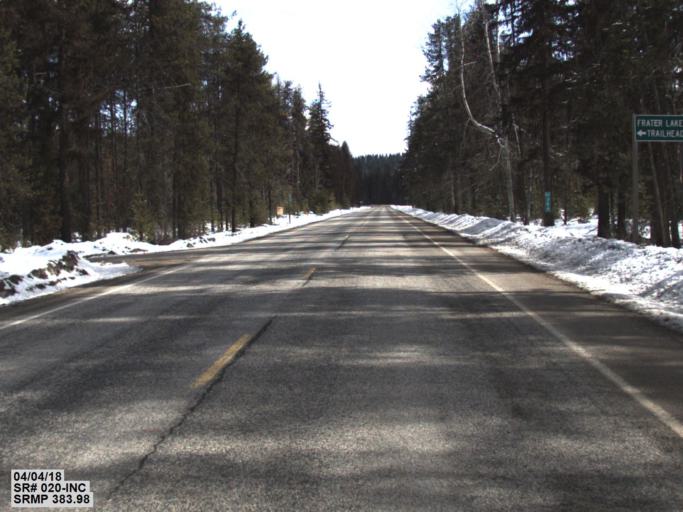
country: US
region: Washington
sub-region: Stevens County
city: Colville
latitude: 48.6542
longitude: -117.4839
